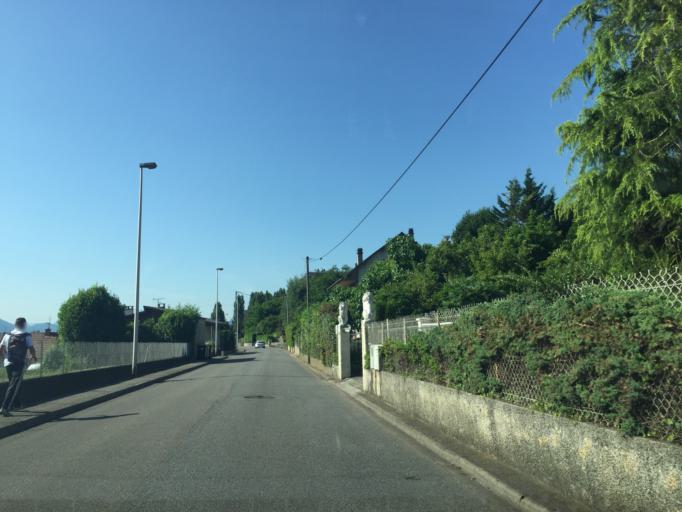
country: FR
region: Rhone-Alpes
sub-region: Departement de la Savoie
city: Drumettaz-Clarafond
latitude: 45.6720
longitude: 5.9148
